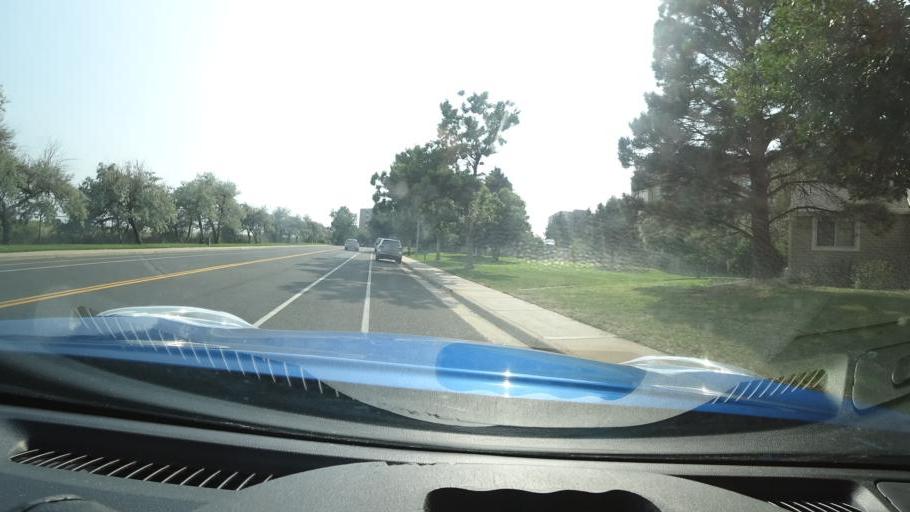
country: US
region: Colorado
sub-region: Adams County
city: Aurora
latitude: 39.6644
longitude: -104.8227
